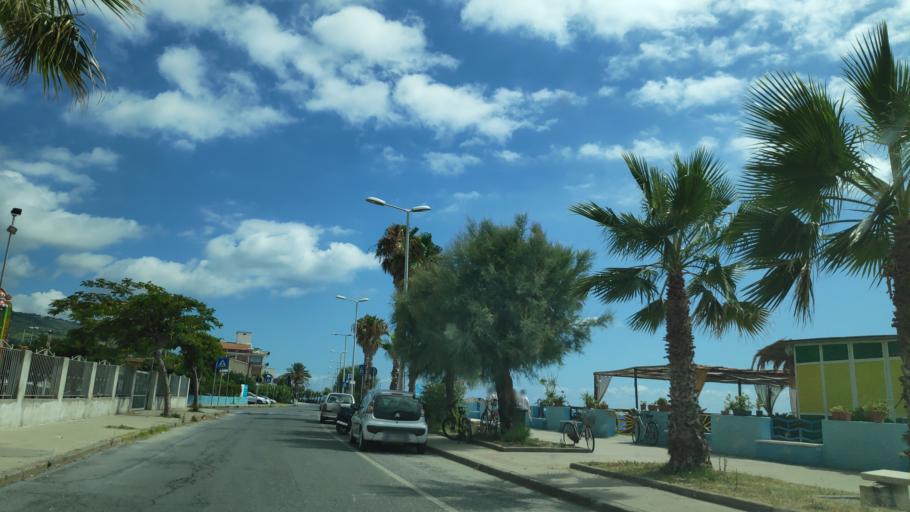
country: IT
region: Calabria
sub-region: Provincia di Cosenza
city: Amantea
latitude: 39.1309
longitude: 16.0692
